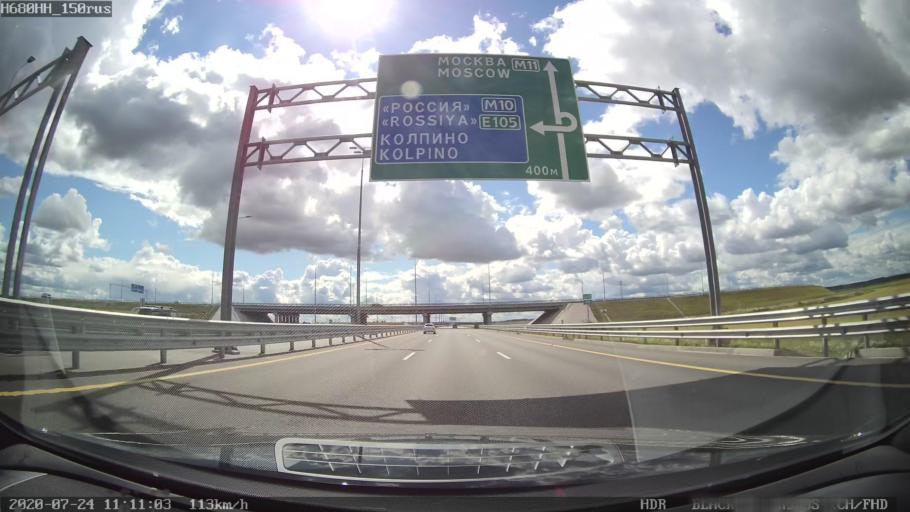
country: RU
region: St.-Petersburg
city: Tyarlevo
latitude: 59.7286
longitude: 30.5108
